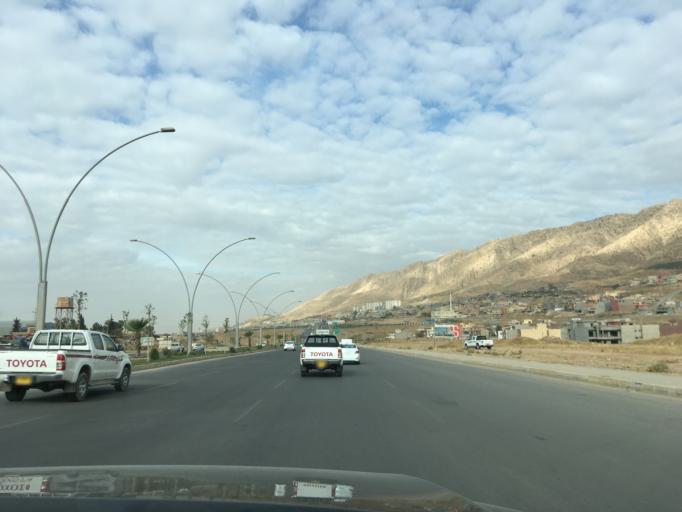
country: IQ
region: Dahuk
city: Sinah
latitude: 36.8463
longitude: 43.0601
